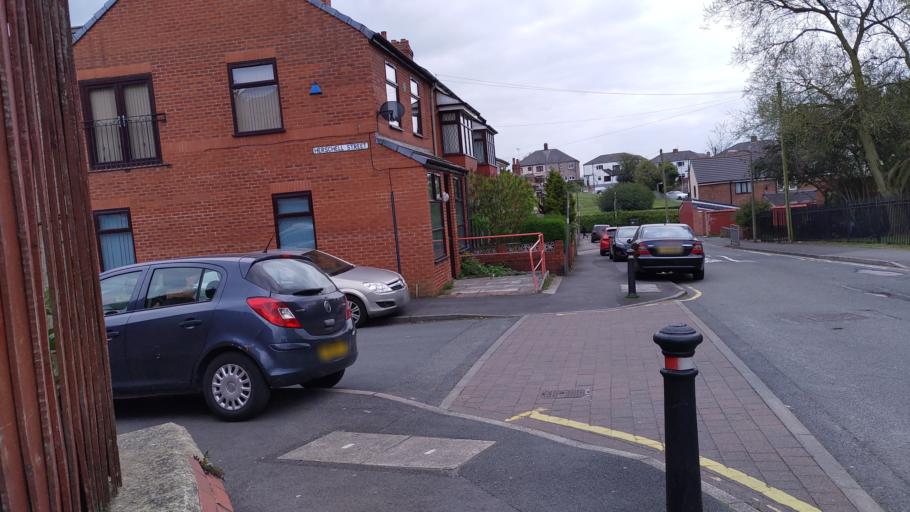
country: GB
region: England
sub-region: Lancashire
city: Preston
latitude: 53.7541
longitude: -2.6926
